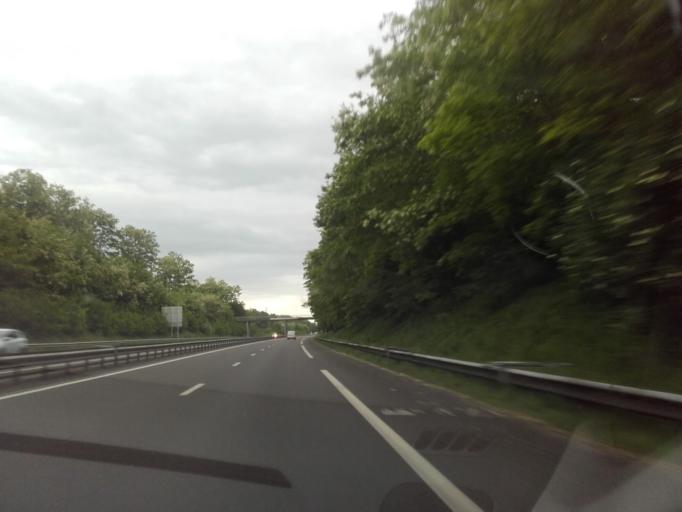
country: FR
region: Auvergne
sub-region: Departement du Puy-de-Dome
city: Lezoux
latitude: 45.8522
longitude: 3.3903
